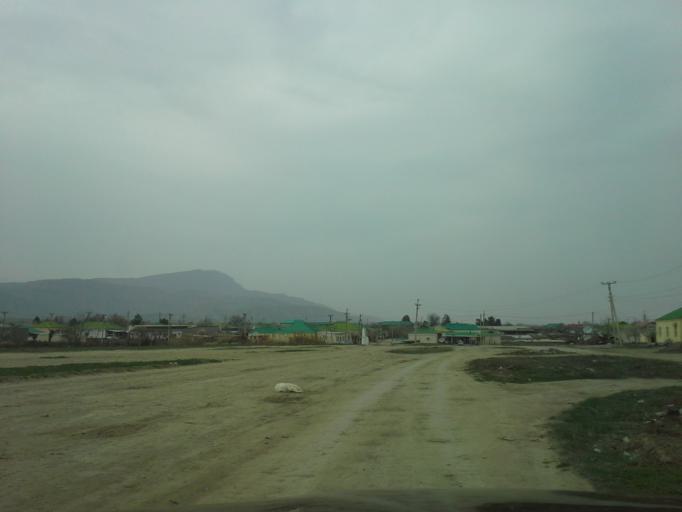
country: TM
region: Ahal
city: Abadan
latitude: 37.9714
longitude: 58.2231
